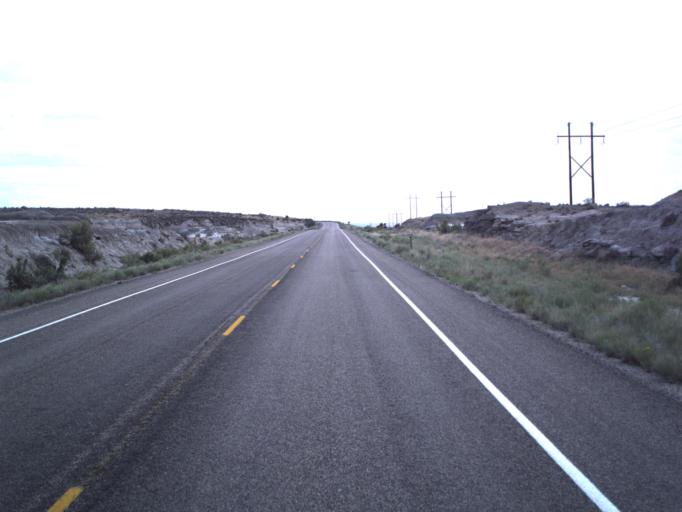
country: US
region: Colorado
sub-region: Rio Blanco County
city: Rangely
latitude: 40.1022
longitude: -109.2265
